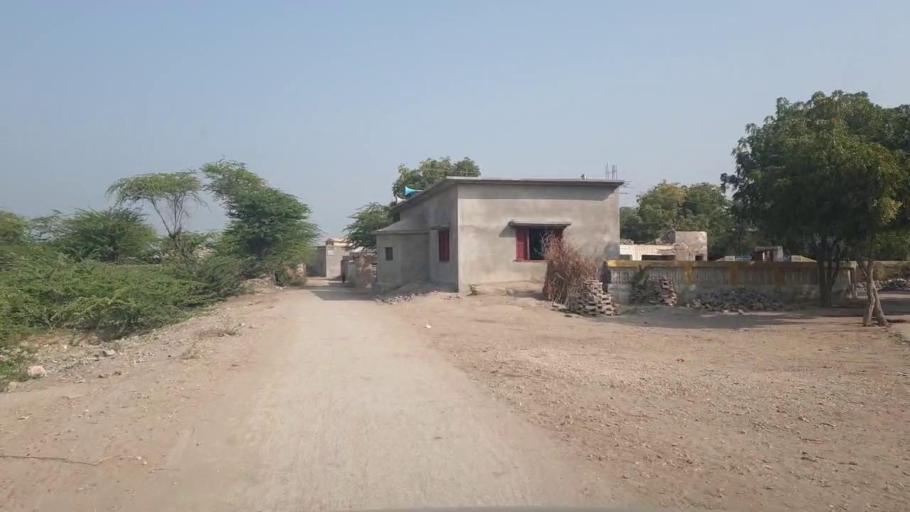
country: PK
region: Sindh
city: Umarkot
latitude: 25.3825
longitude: 69.7309
